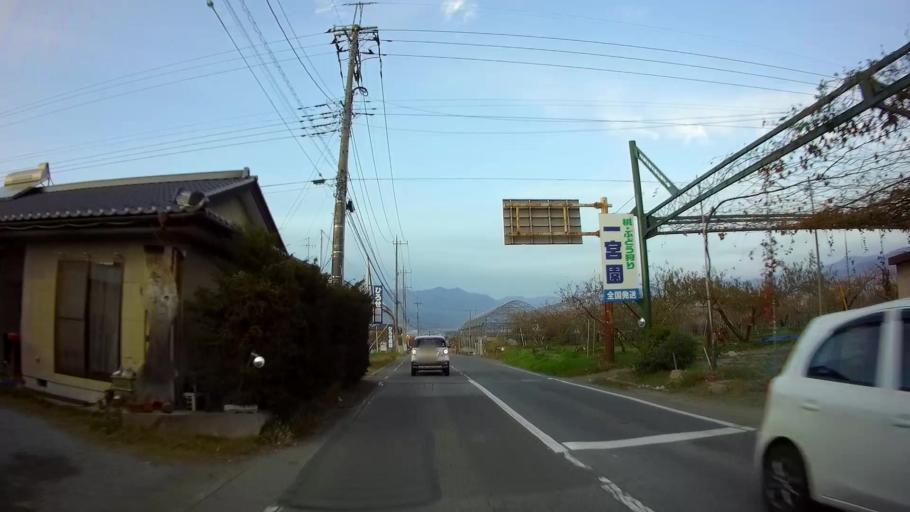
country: JP
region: Yamanashi
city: Isawa
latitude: 35.6449
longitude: 138.6867
